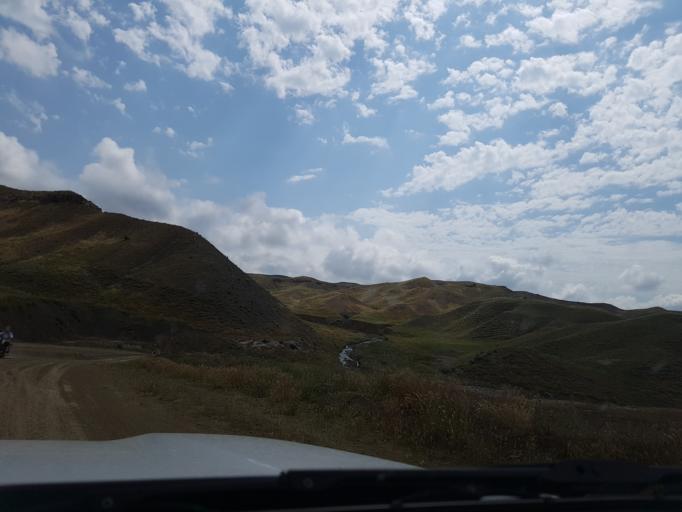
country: TM
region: Balkan
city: Magtymguly
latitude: 38.2659
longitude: 56.7903
